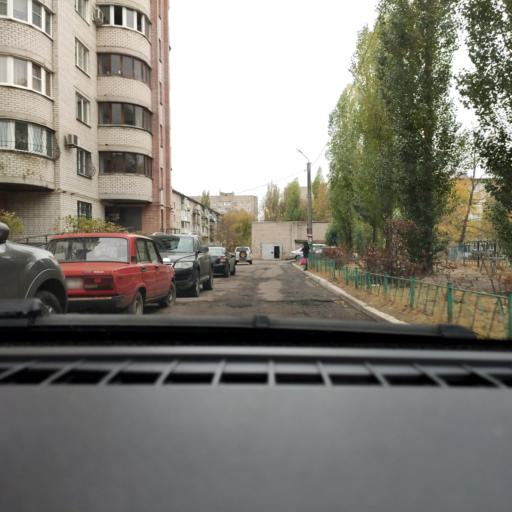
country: RU
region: Voronezj
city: Voronezh
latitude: 51.6826
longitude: 39.2666
